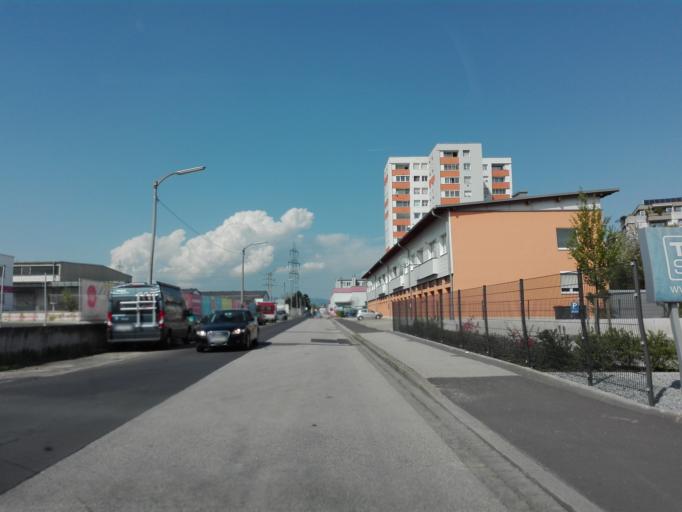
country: AT
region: Upper Austria
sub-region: Politischer Bezirk Linz-Land
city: Ansfelden
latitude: 48.2411
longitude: 14.2763
